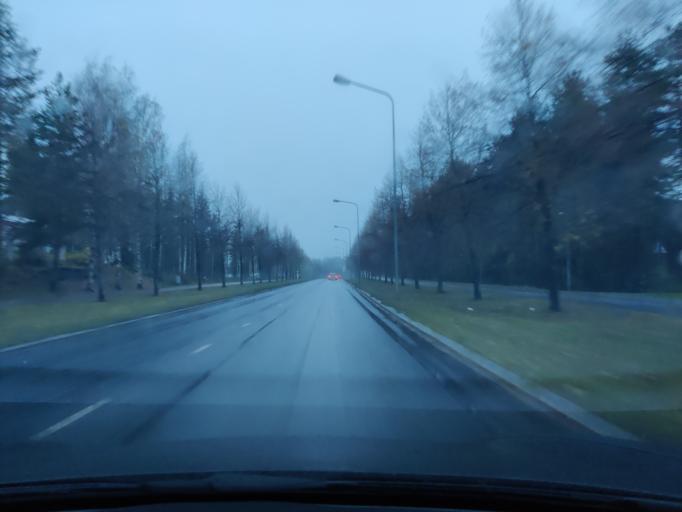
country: FI
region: Northern Savo
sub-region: Kuopio
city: Kuopio
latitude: 62.8351
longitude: 27.6631
